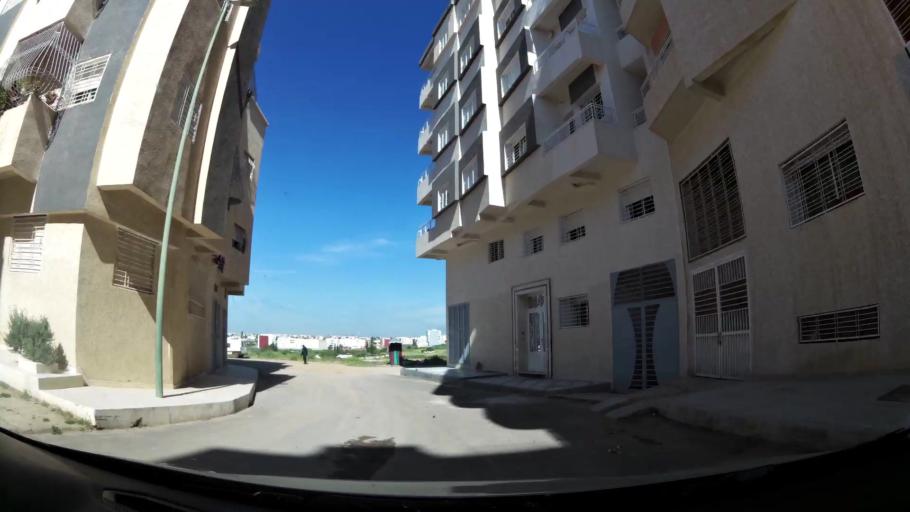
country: MA
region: Fes-Boulemane
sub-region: Fes
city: Fes
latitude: 33.9990
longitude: -5.0040
